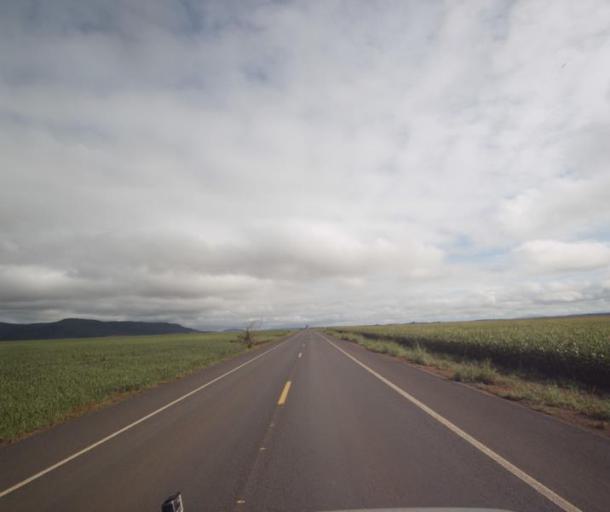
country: BR
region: Goias
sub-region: Padre Bernardo
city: Padre Bernardo
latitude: -15.4111
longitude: -48.6272
